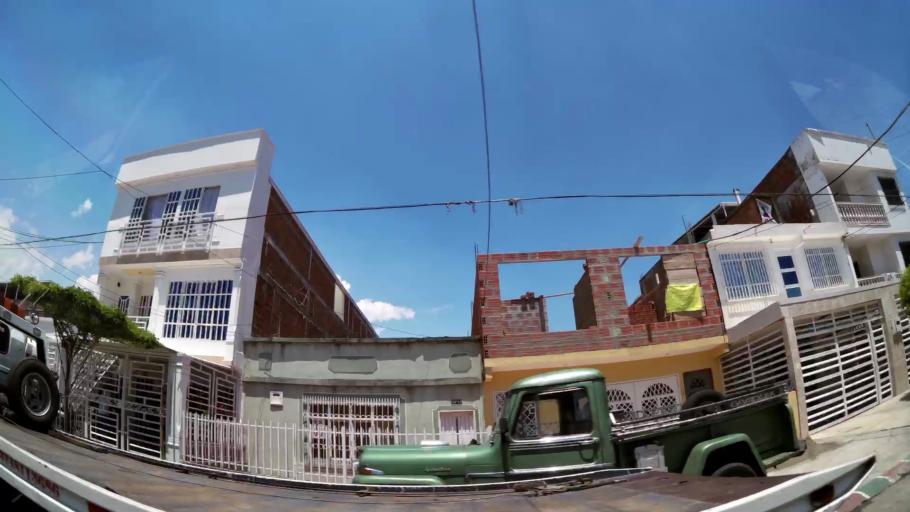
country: CO
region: Valle del Cauca
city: Cali
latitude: 3.4320
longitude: -76.5067
